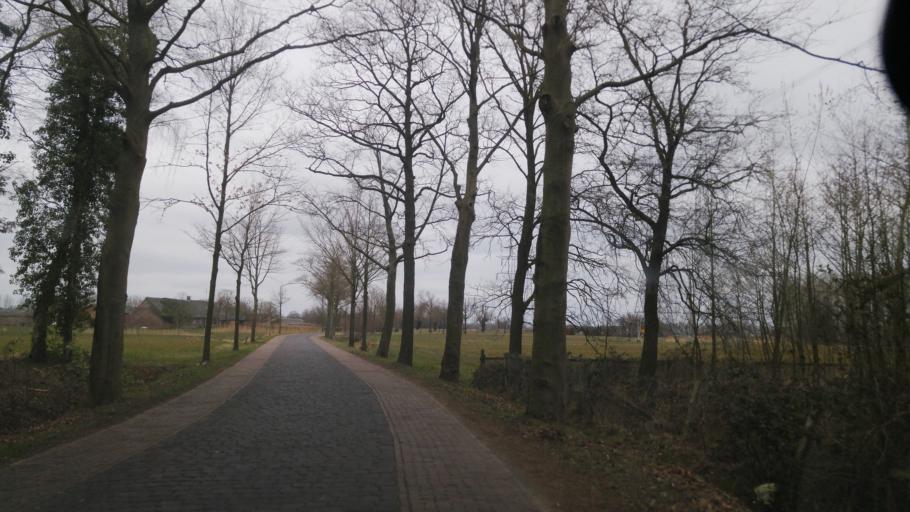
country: NL
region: North Brabant
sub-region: Gemeente Eindhoven
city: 't Hofke
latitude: 51.4731
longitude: 5.5167
